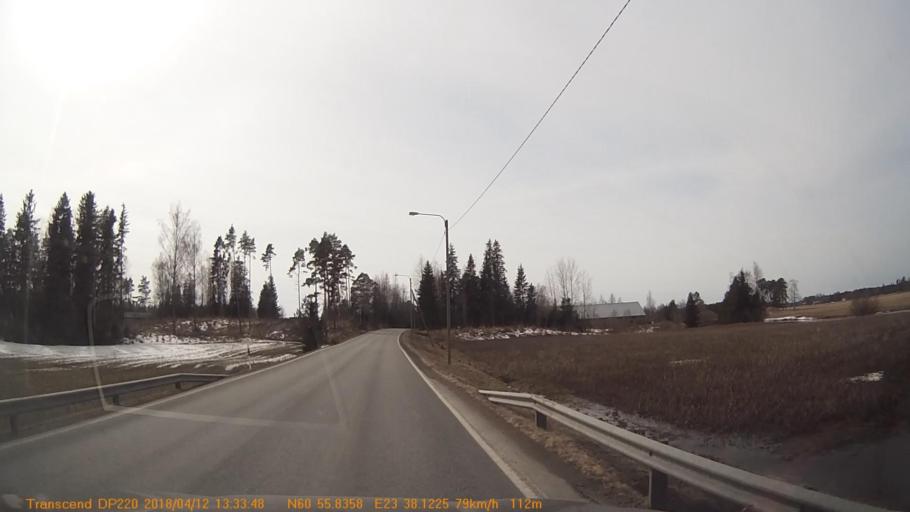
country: FI
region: Haeme
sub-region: Forssa
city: Forssa
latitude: 60.9305
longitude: 23.6352
